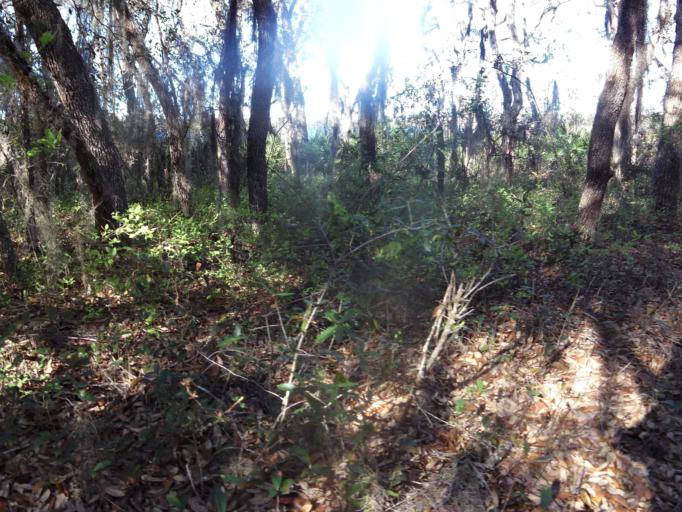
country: US
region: Florida
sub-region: Clay County
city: Keystone Heights
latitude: 29.8205
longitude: -82.0216
